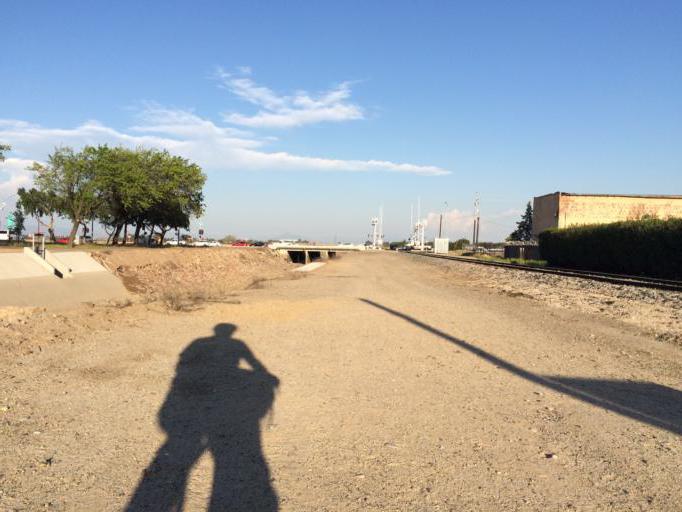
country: US
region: California
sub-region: Fresno County
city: Sunnyside
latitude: 36.7649
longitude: -119.7019
